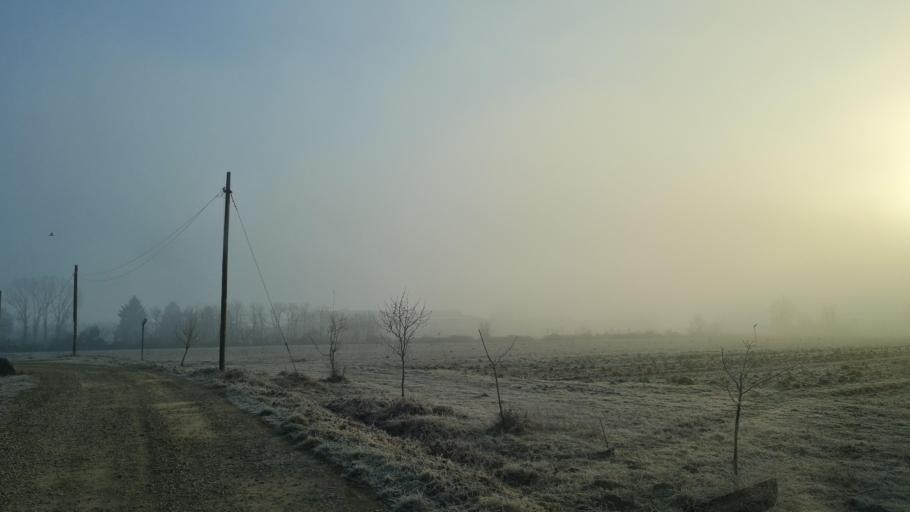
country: IT
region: Piedmont
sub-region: Provincia di Biella
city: Vergnasco
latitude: 45.4692
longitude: 8.0911
